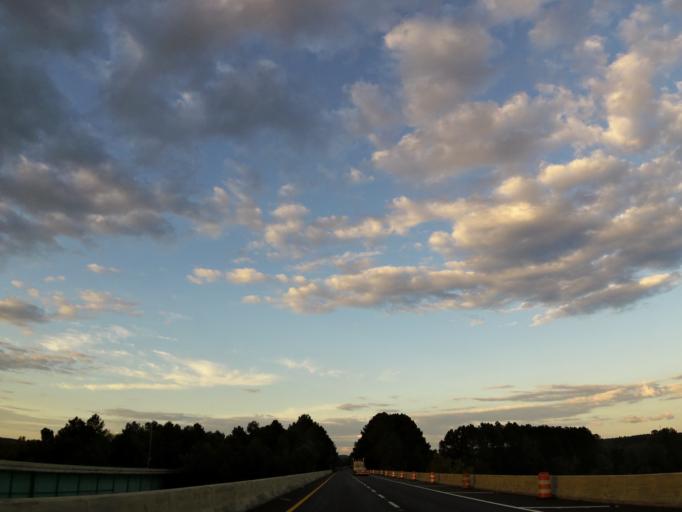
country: US
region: Tennessee
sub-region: Bradley County
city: Hopewell
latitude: 35.3157
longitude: -84.7993
